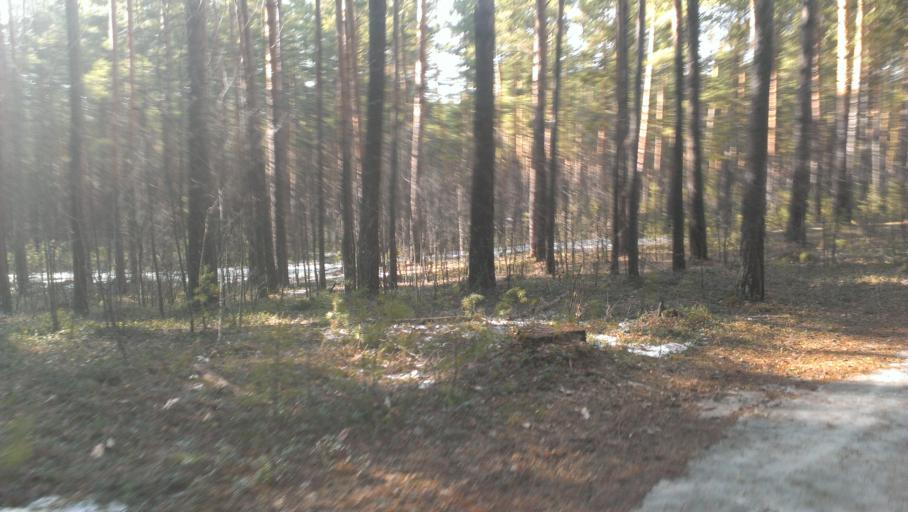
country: RU
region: Altai Krai
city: Yuzhnyy
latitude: 53.2837
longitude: 83.6993
